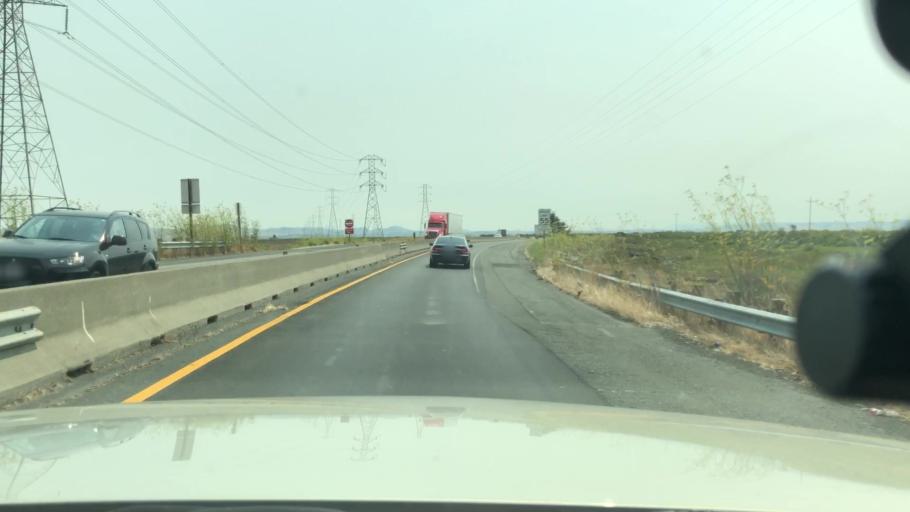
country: US
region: California
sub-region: Marin County
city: Black Point-Green Point
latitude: 38.1553
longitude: -122.4025
